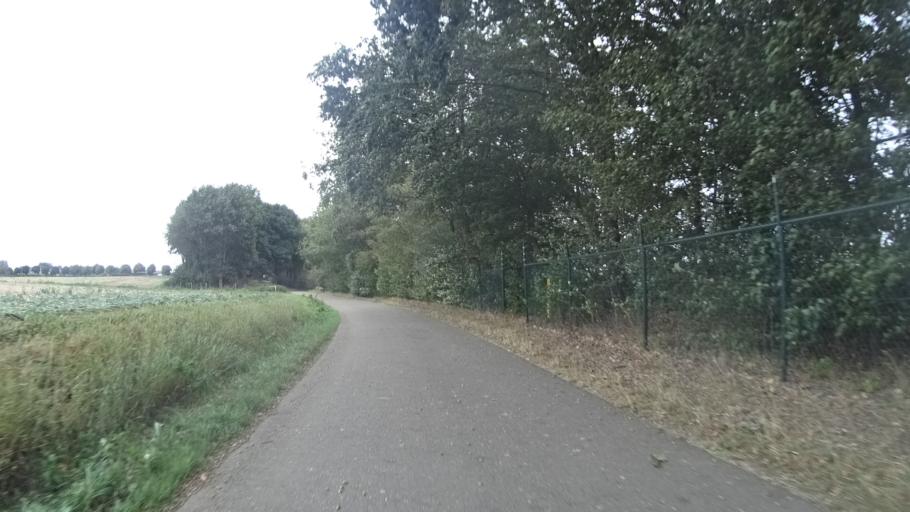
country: NL
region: Limburg
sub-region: Gemeente Beesel
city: Beesel
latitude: 51.2771
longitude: 6.0284
